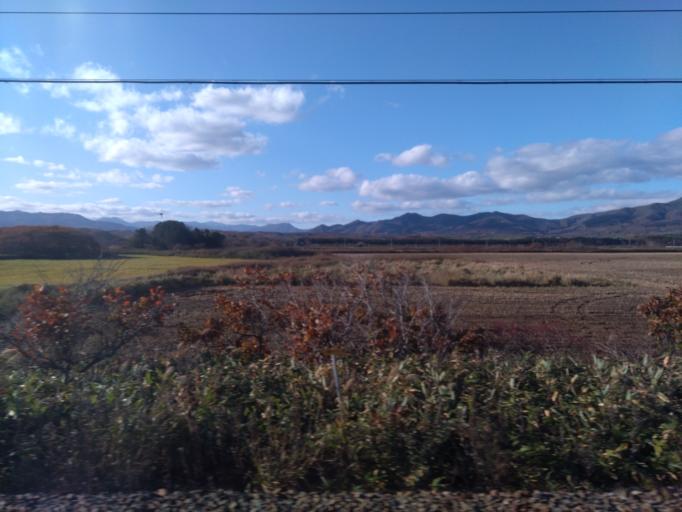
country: JP
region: Hokkaido
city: Niseko Town
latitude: 42.5398
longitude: 140.4054
